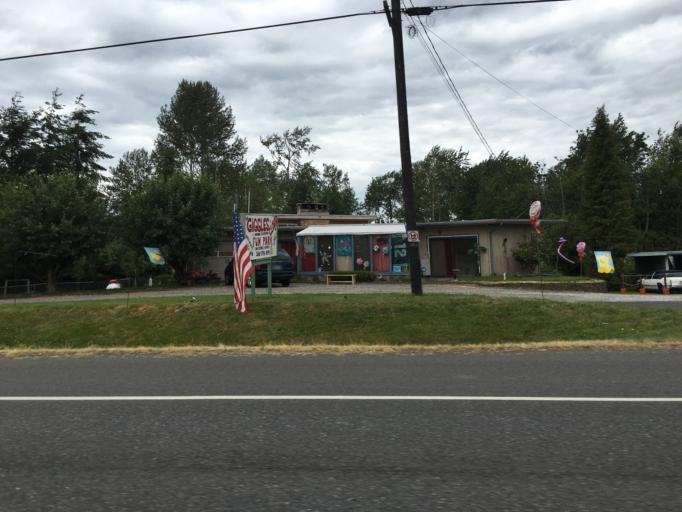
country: US
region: Washington
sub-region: Whatcom County
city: Bellingham
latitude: 48.8233
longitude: -122.4861
